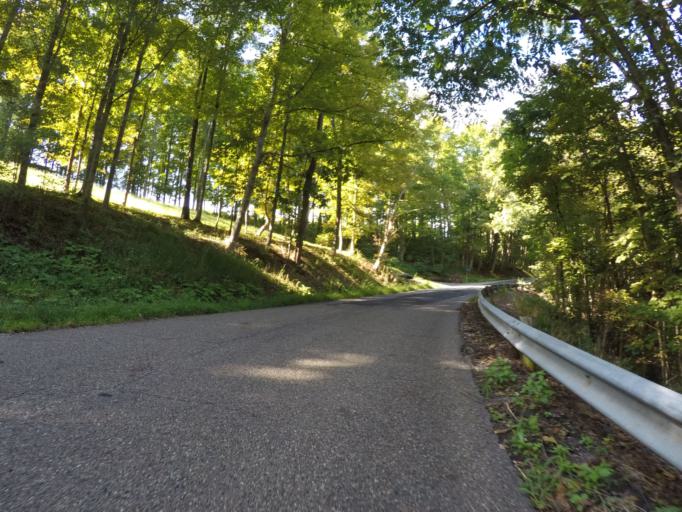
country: US
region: West Virginia
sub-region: Cabell County
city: Huntington
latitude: 38.4673
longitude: -82.4605
